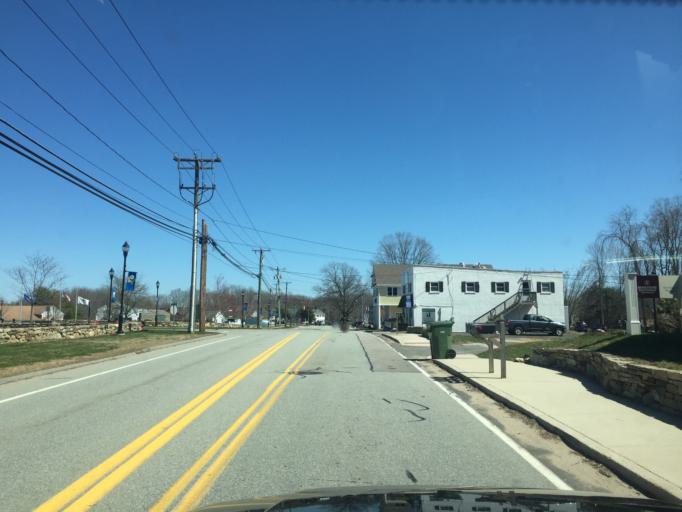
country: US
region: Connecticut
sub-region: Hartford County
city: Terramuggus
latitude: 41.6323
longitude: -72.4622
